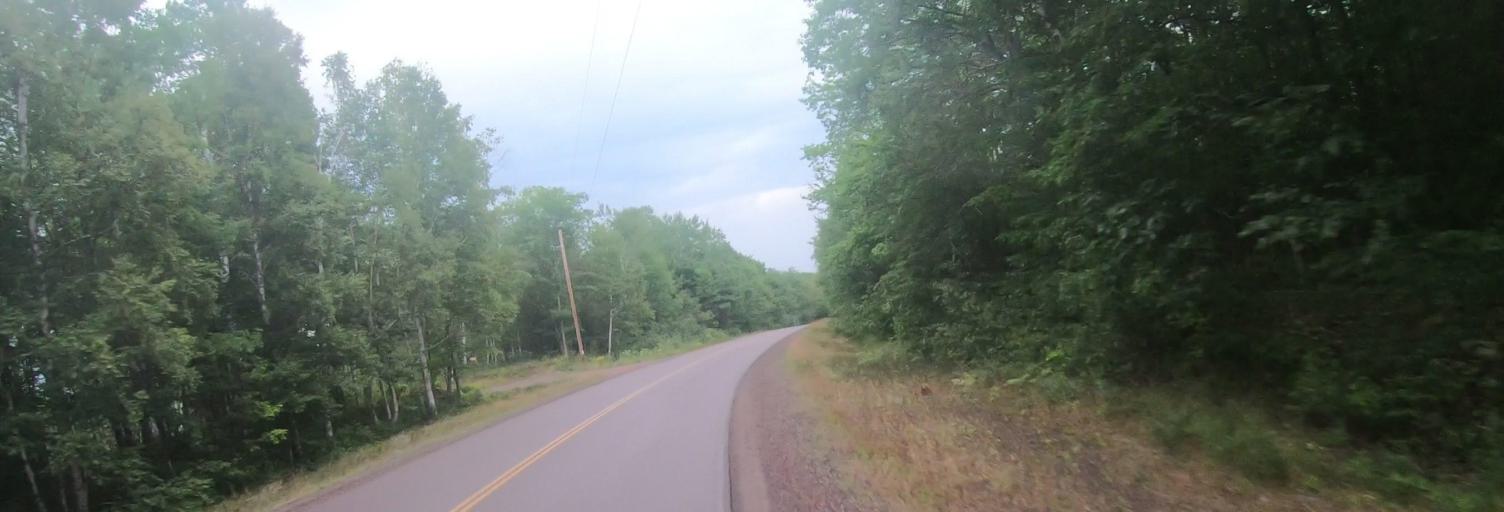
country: US
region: Michigan
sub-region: Keweenaw County
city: Eagle River
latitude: 47.2985
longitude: -88.3364
